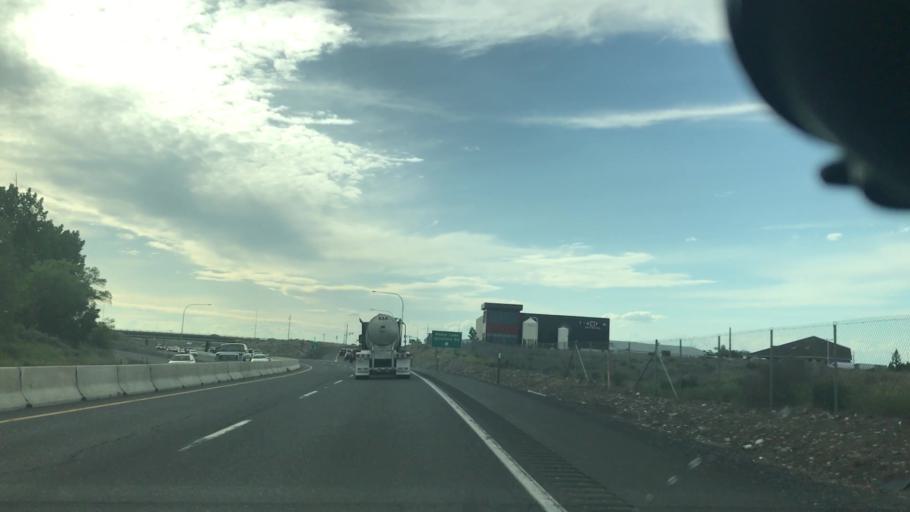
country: US
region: Washington
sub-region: Grant County
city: Moses Lake
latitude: 47.1429
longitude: -119.2733
